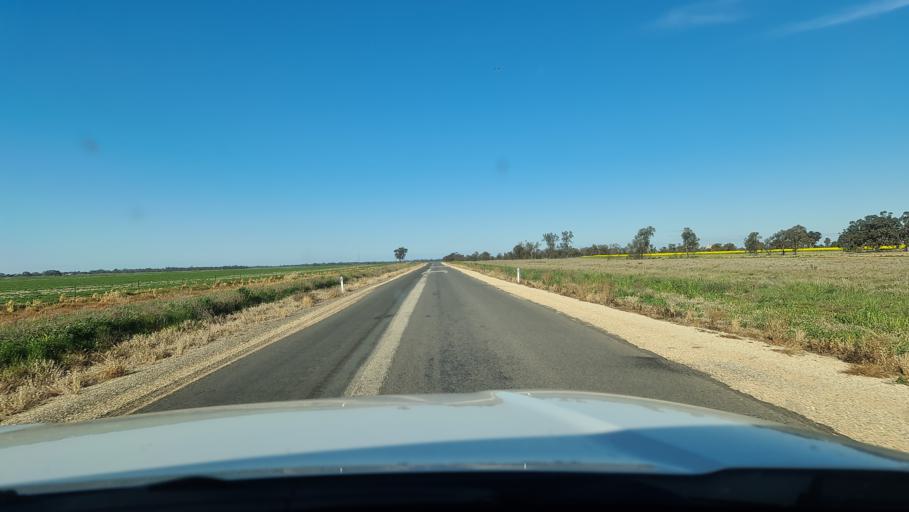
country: AU
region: Victoria
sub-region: Horsham
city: Horsham
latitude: -36.4492
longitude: 142.5539
